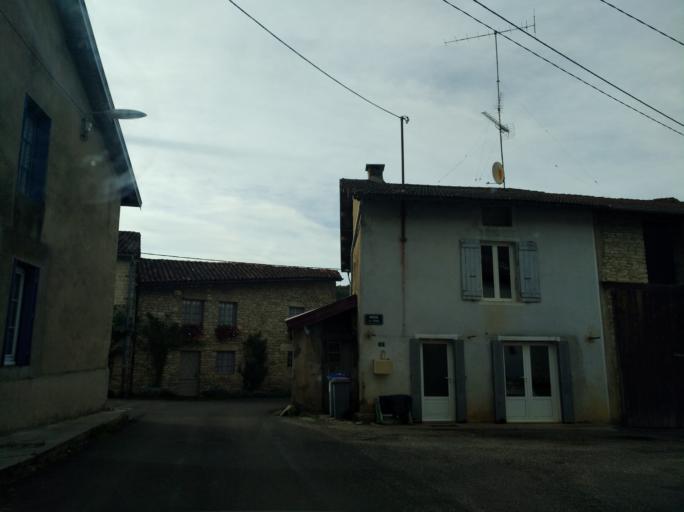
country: FR
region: Bourgogne
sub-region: Departement de Saone-et-Loire
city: Cuiseaux
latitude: 46.4695
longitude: 5.4518
